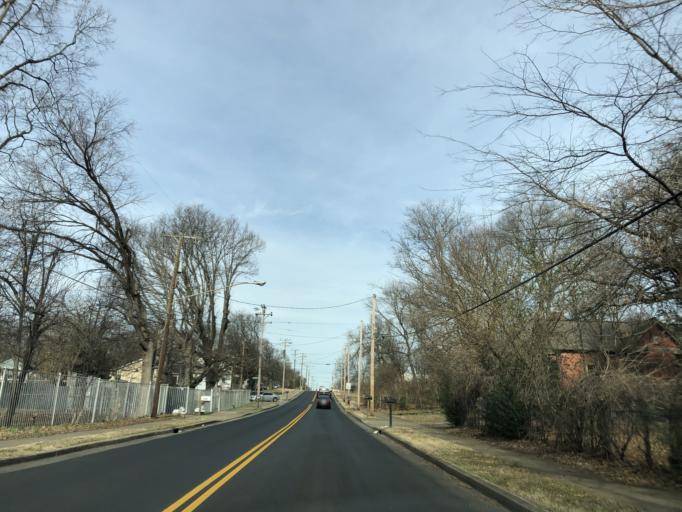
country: US
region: Tennessee
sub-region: Davidson County
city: Nashville
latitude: 36.2003
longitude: -86.7621
